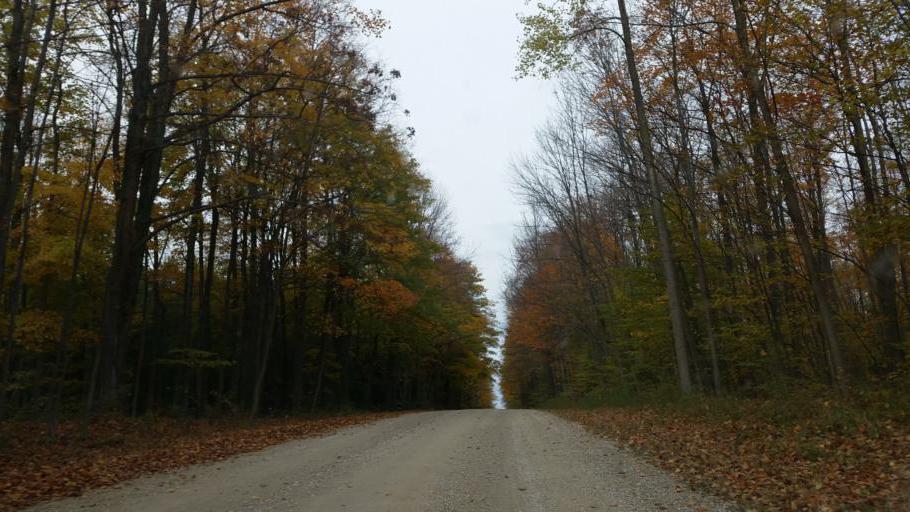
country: CA
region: Ontario
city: Wingham
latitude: 43.9844
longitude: -81.3346
